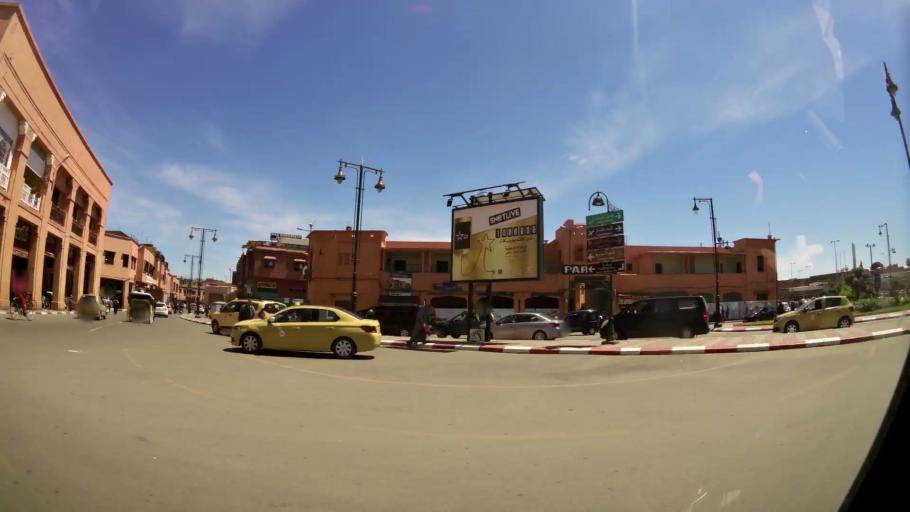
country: MA
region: Marrakech-Tensift-Al Haouz
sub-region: Marrakech
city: Marrakesh
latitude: 31.6225
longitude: -7.9918
